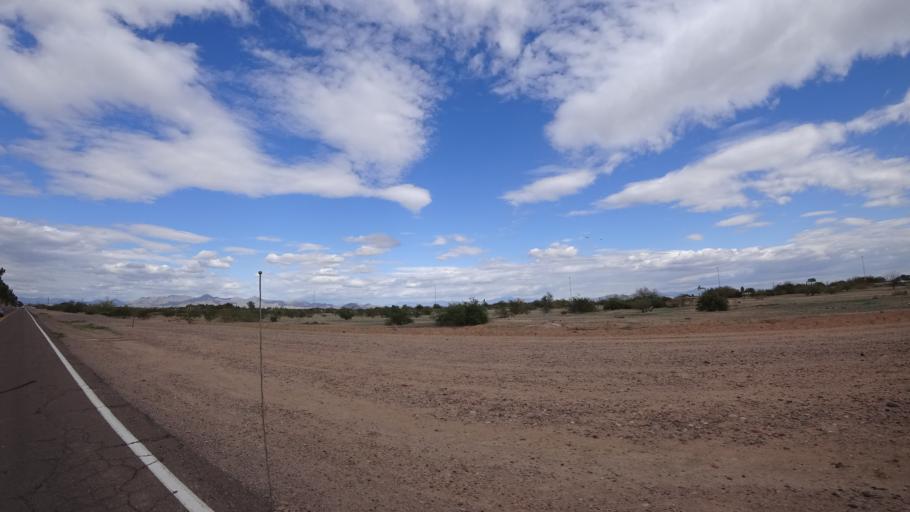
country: US
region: Arizona
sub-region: Maricopa County
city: Scottsdale
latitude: 33.4738
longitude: -111.8918
